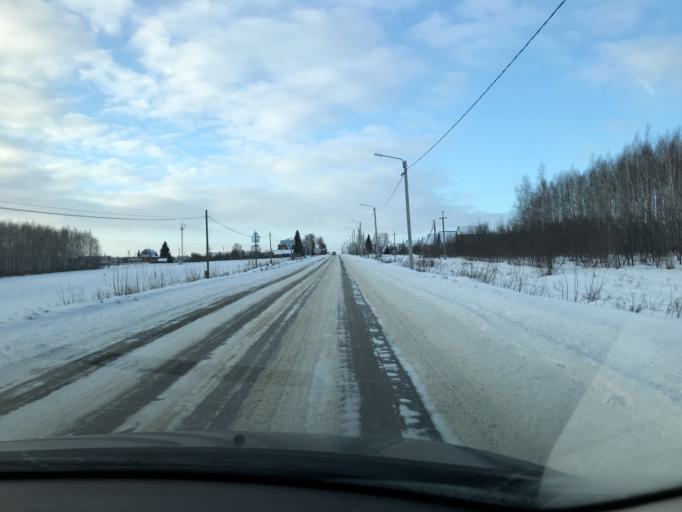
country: RU
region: Ulyanovsk
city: Undory
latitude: 54.6024
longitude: 48.4174
